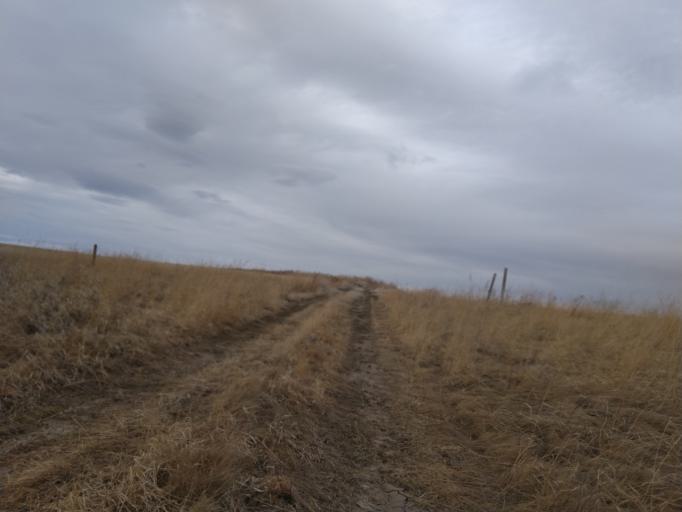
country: CA
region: Alberta
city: Calgary
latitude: 51.1759
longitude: -114.0659
